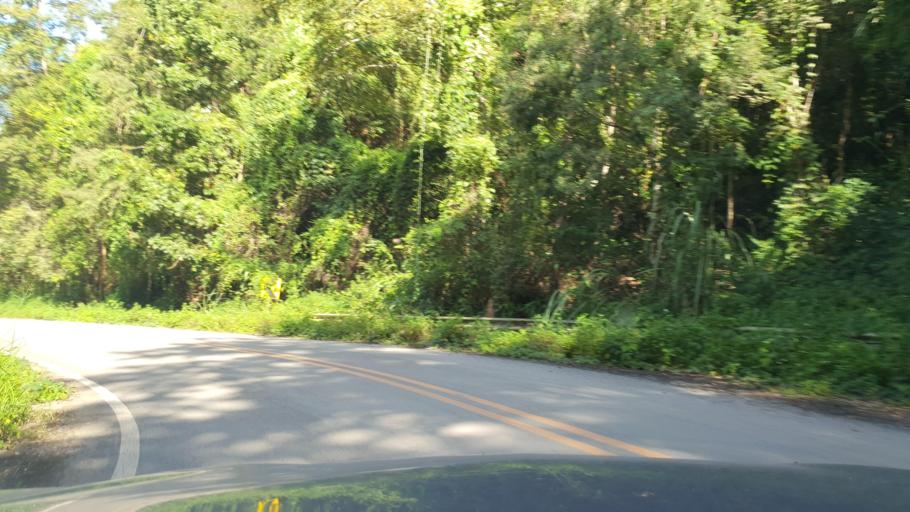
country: TH
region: Chiang Rai
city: Wiang Pa Pao
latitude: 19.3270
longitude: 99.4452
